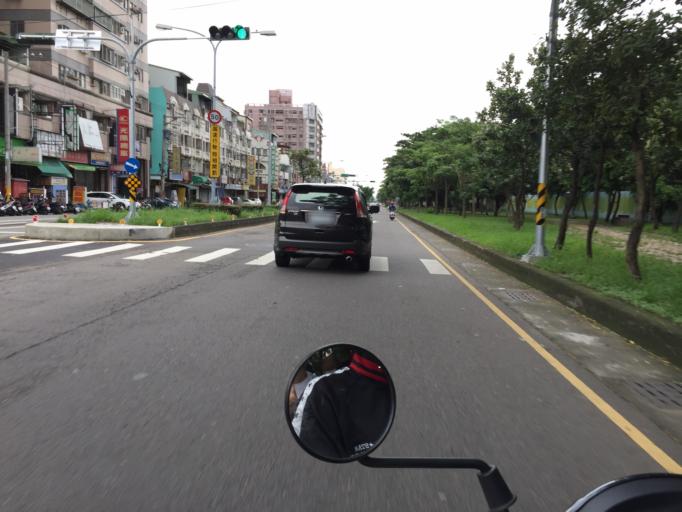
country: TW
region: Taiwan
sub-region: Taichung City
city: Taichung
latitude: 24.1544
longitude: 120.6987
